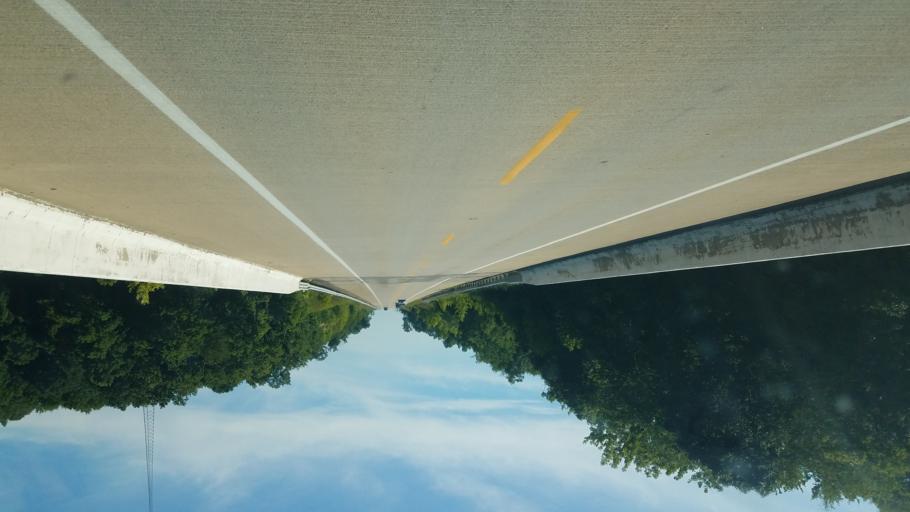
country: US
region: Ohio
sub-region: Meigs County
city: Pomeroy
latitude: 39.1718
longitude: -82.0424
